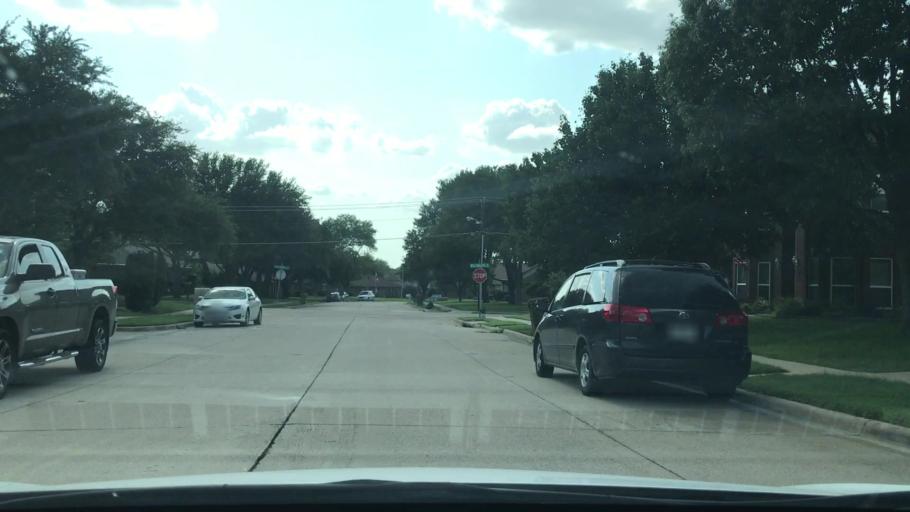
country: US
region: Texas
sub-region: Dallas County
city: Carrollton
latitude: 32.9733
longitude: -96.8637
